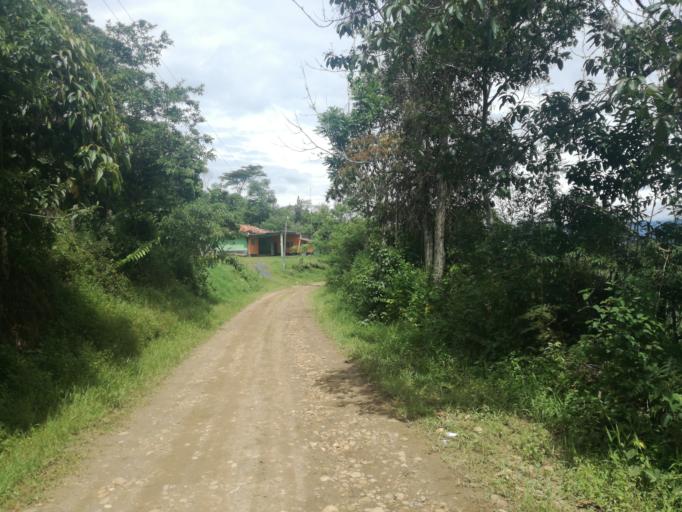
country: CO
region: Boyaca
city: Santana
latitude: 6.0538
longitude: -73.4877
